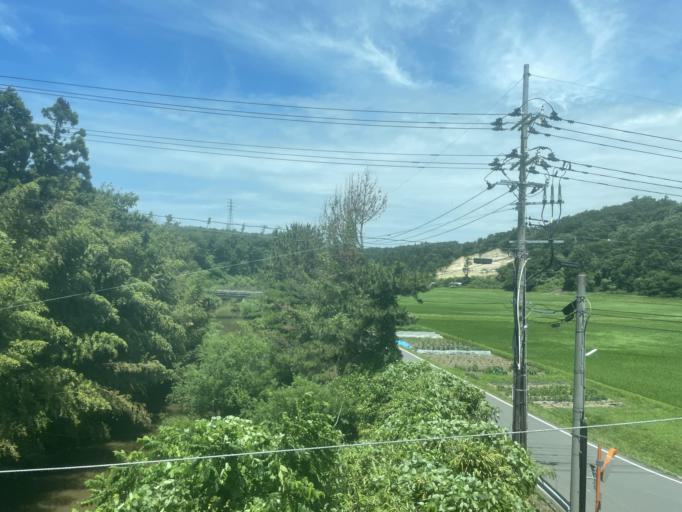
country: JP
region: Yamagata
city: Yuza
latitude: 39.3504
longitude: 140.0277
